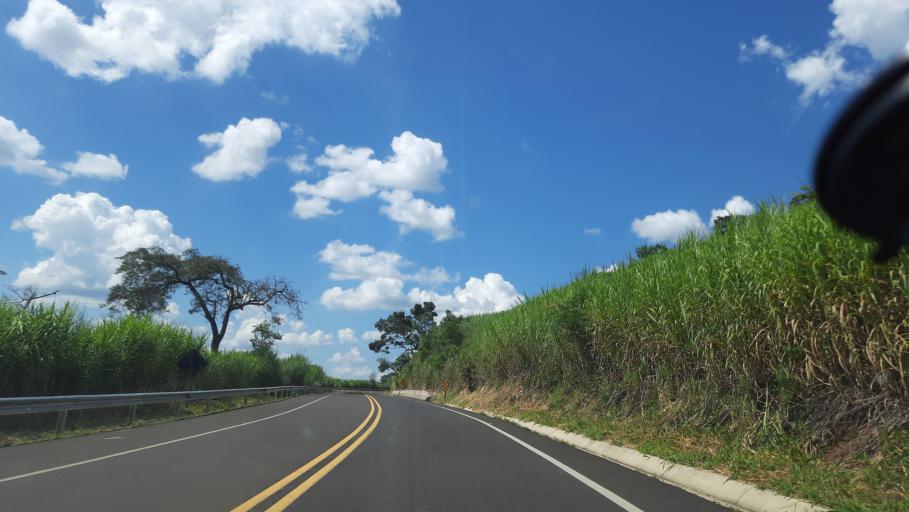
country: BR
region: Sao Paulo
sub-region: Sao Jose Do Rio Pardo
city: Sao Jose do Rio Pardo
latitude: -21.6011
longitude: -46.9385
